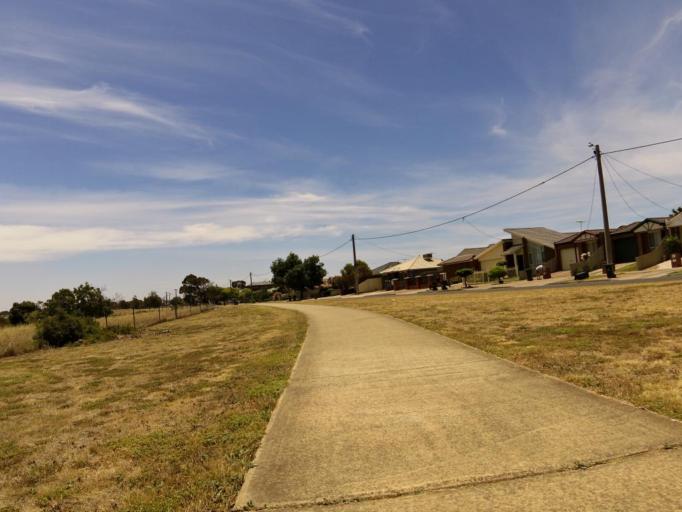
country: AU
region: Victoria
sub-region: Hobsons Bay
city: Laverton
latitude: -37.8787
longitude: 144.7661
